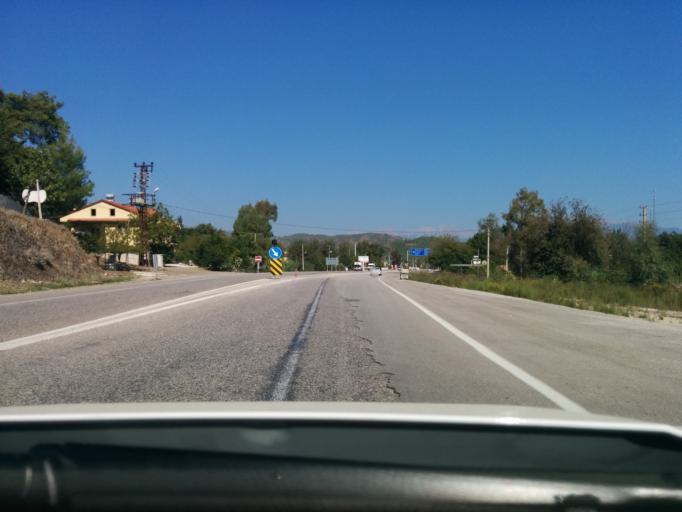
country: TR
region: Mugla
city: Kemer
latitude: 36.6290
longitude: 29.3563
